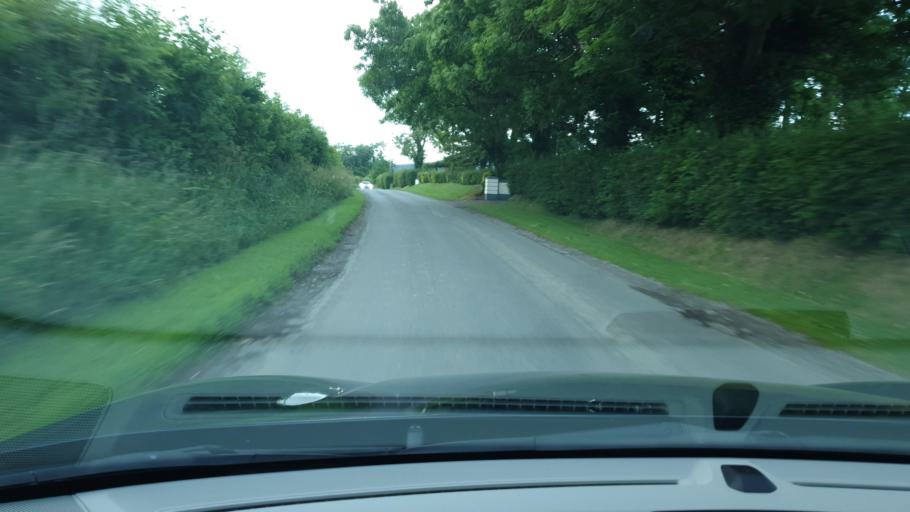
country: IE
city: Kentstown
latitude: 53.5712
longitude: -6.4951
